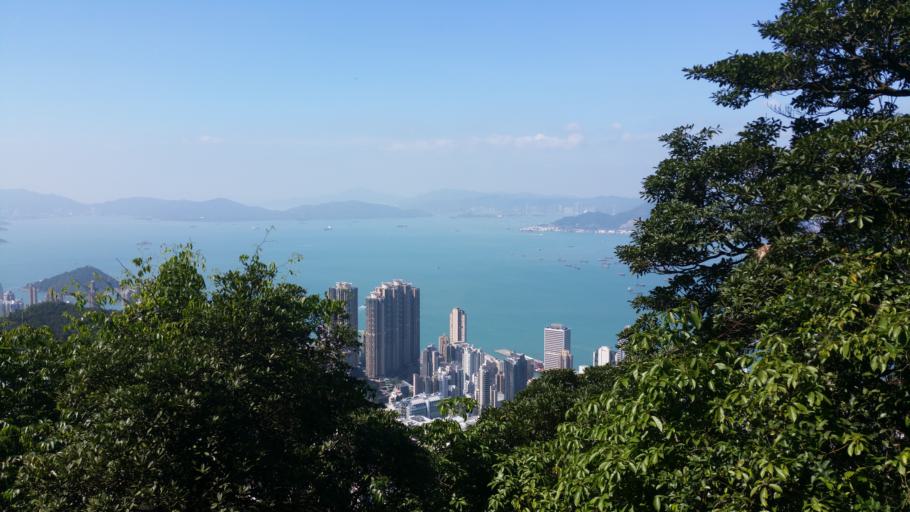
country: HK
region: Central and Western
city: Central
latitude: 22.2782
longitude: 114.1449
